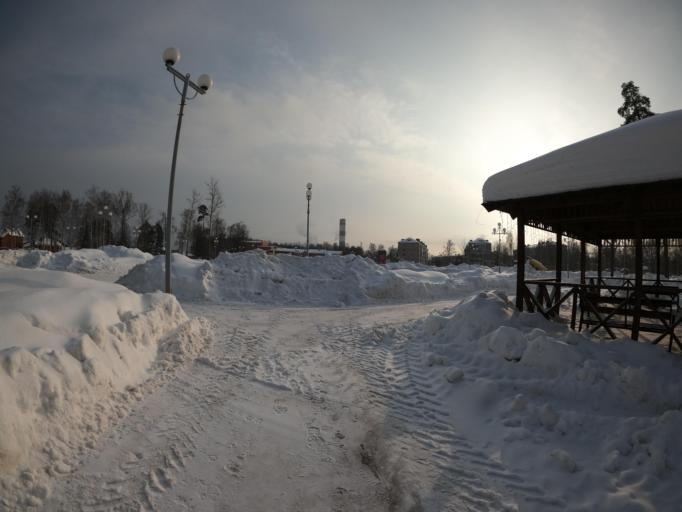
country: RU
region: Moskovskaya
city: Elektrogorsk
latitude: 55.8946
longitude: 38.7724
